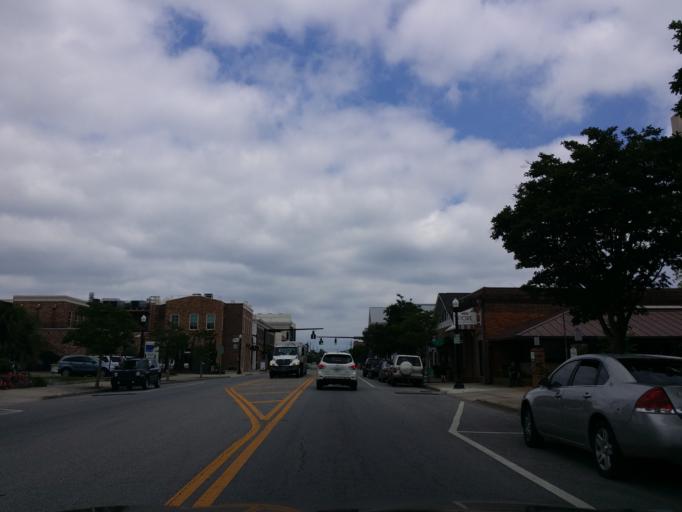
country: US
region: Florida
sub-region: Escambia County
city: Pensacola
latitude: 30.4074
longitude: -87.2153
